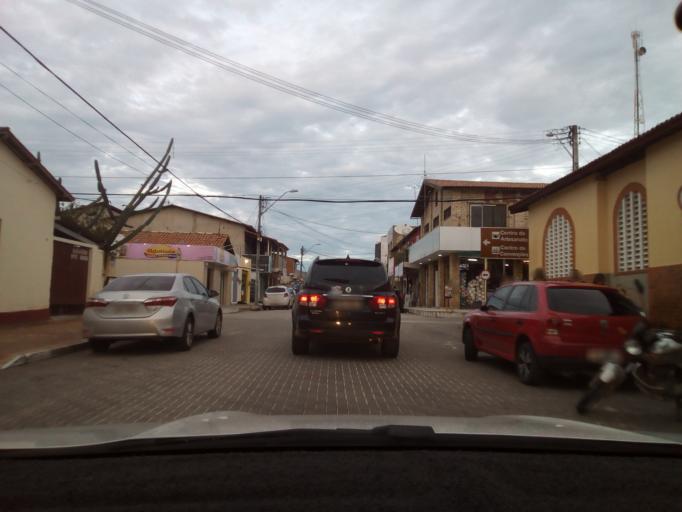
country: BR
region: Ceara
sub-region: Beberibe
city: Beberibe
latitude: -4.1813
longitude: -38.1295
